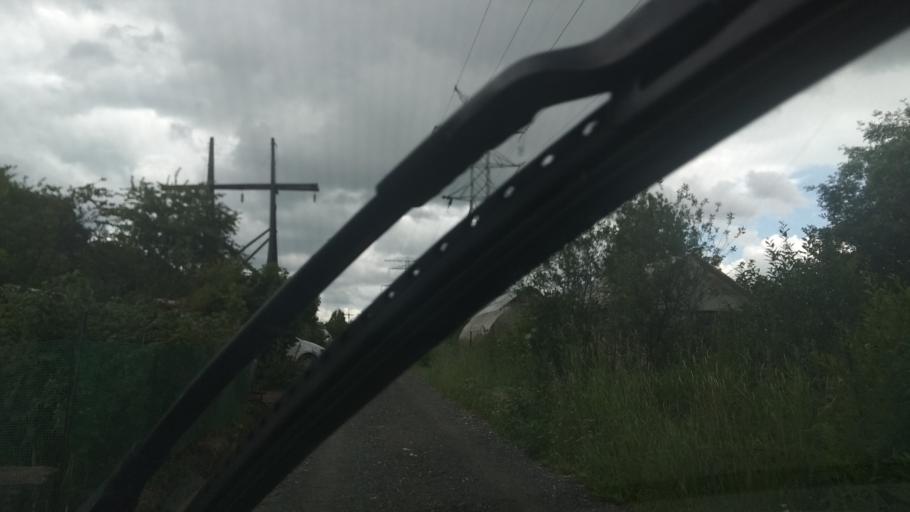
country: RU
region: Sverdlovsk
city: Verkhnyaya Pyshma
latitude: 56.9198
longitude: 60.5762
